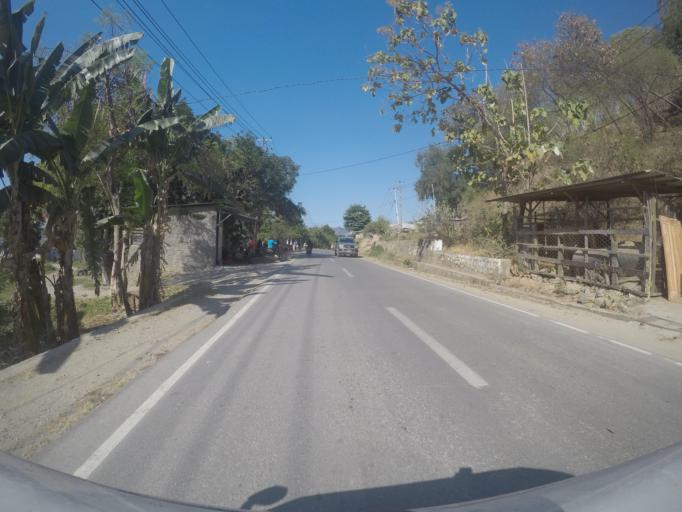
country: TL
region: Dili
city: Dili
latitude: -8.5661
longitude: 125.5499
